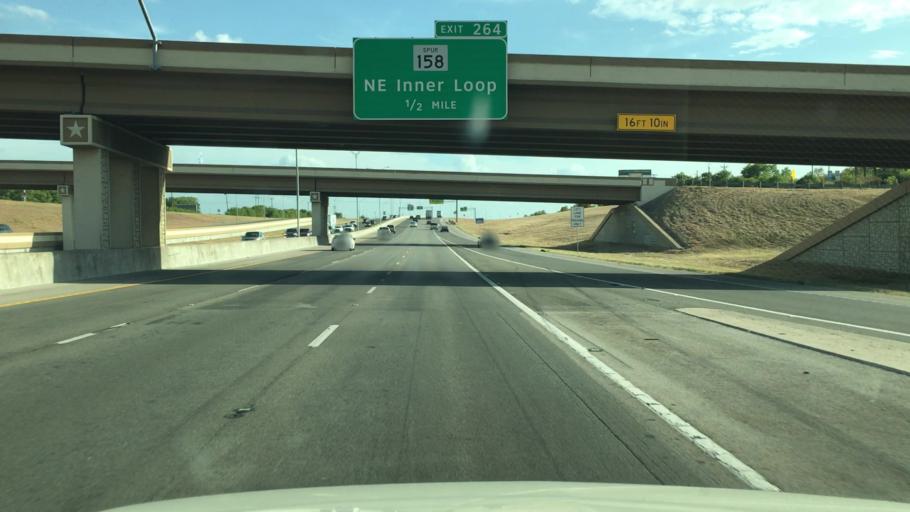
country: US
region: Texas
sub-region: Williamson County
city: Serenada
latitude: 30.6861
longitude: -97.6582
